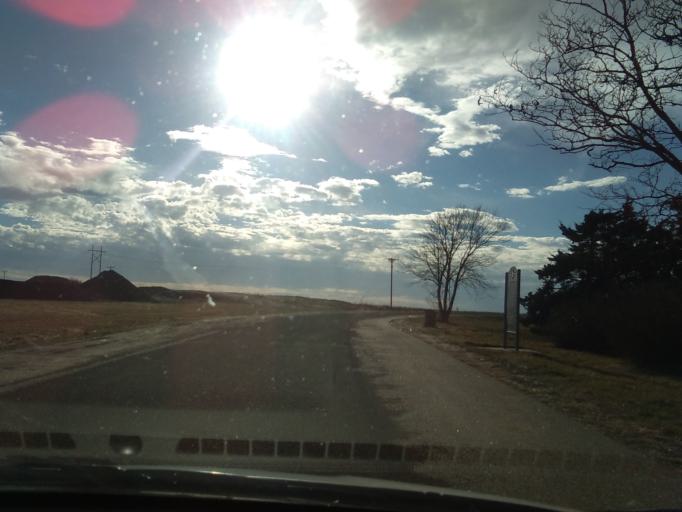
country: US
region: Nebraska
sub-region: Webster County
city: Red Cloud
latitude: 40.2915
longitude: -98.5191
